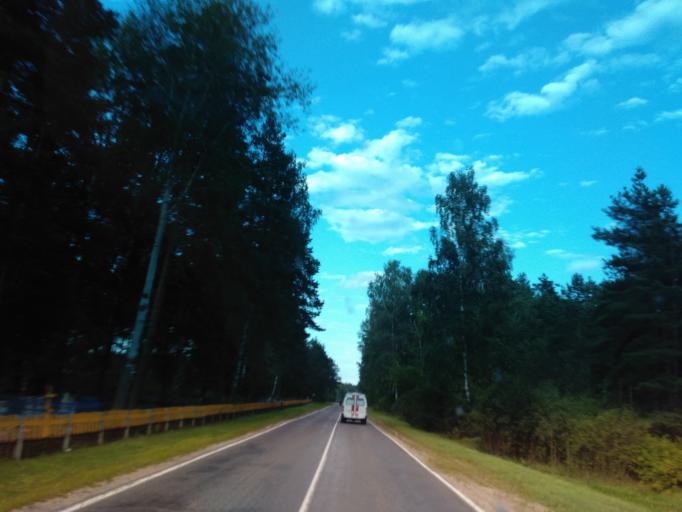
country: BY
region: Minsk
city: Uzda
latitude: 53.4182
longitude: 27.4152
